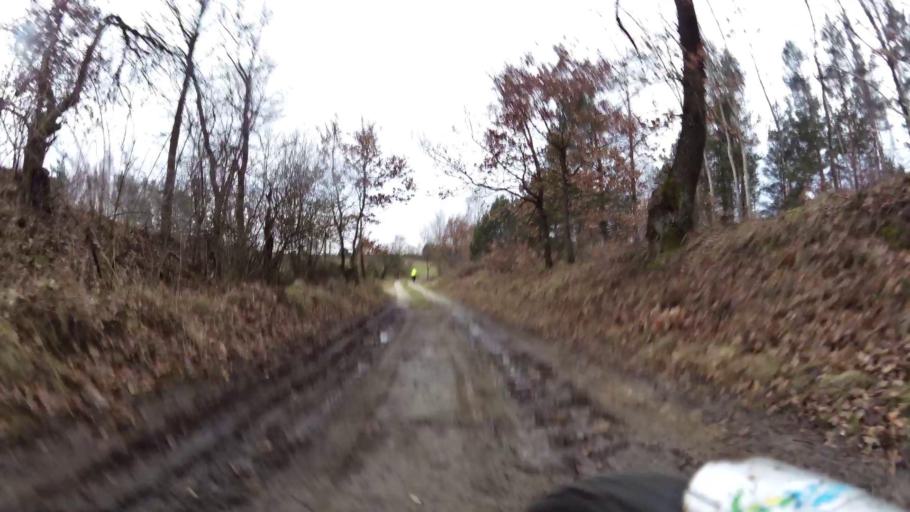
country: PL
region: Pomeranian Voivodeship
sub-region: Powiat bytowski
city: Miastko
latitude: 54.0138
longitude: 16.9991
